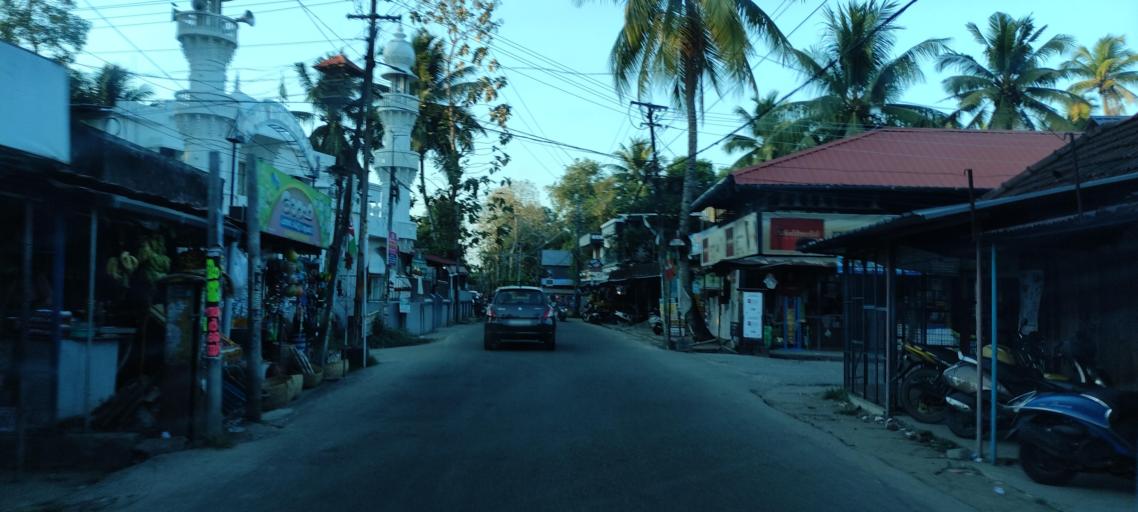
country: IN
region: Kerala
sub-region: Alappuzha
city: Kayankulam
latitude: 9.2373
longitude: 76.4554
